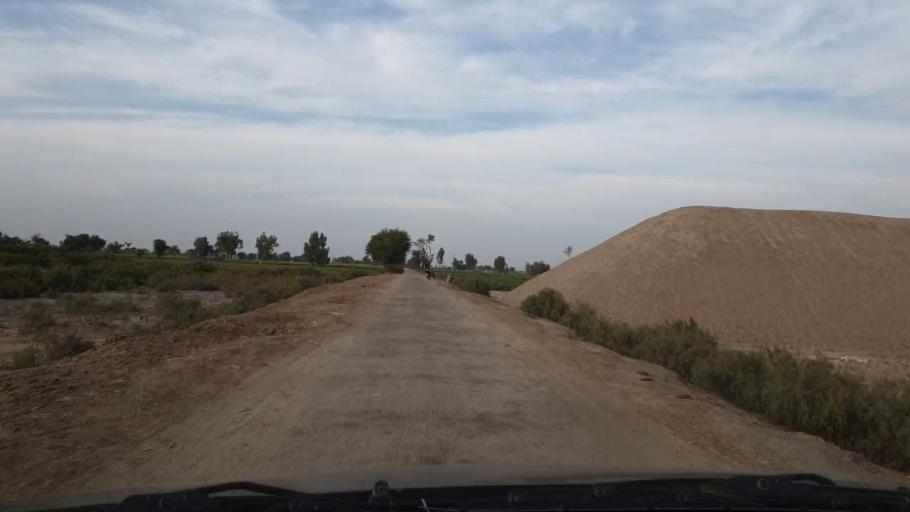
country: PK
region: Sindh
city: Khadro
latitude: 26.1602
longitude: 68.7266
